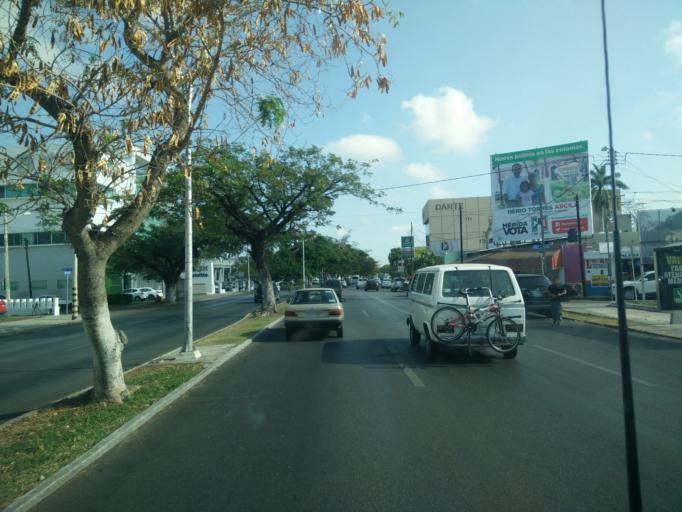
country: MX
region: Yucatan
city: Merida
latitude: 20.9935
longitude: -89.6164
